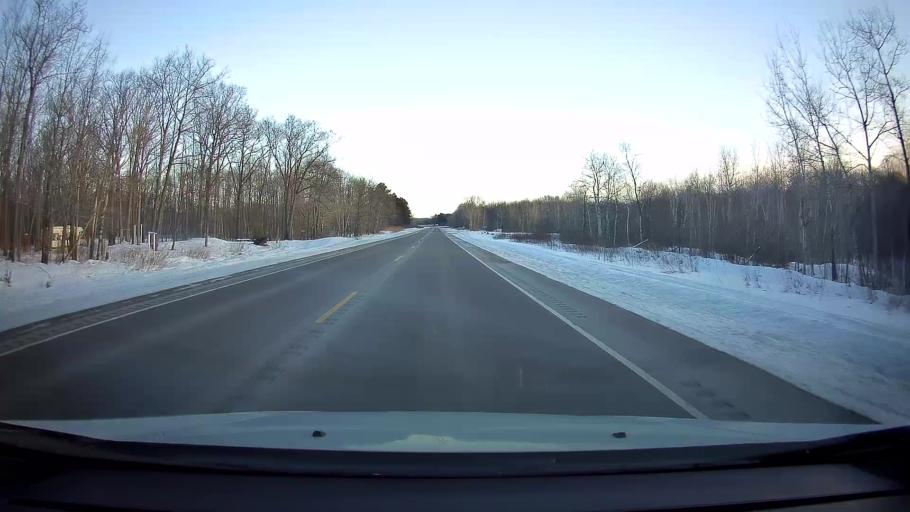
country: US
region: Wisconsin
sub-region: Washburn County
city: Shell Lake
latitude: 45.7024
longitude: -91.9542
